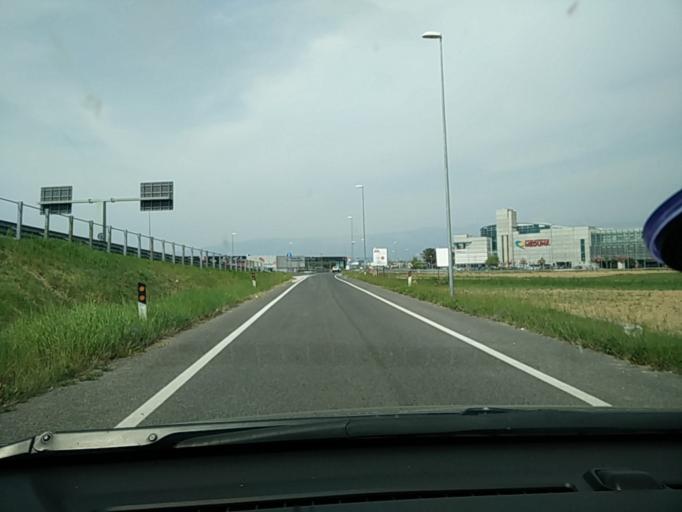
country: IT
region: Friuli Venezia Giulia
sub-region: Provincia di Pordenone
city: Pordenone
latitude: 45.9487
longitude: 12.6931
